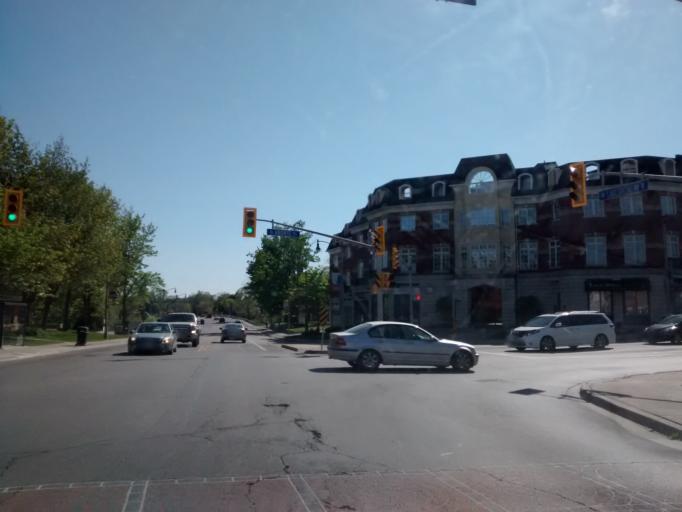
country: CA
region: Ontario
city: Oakville
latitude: 43.3942
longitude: -79.7119
